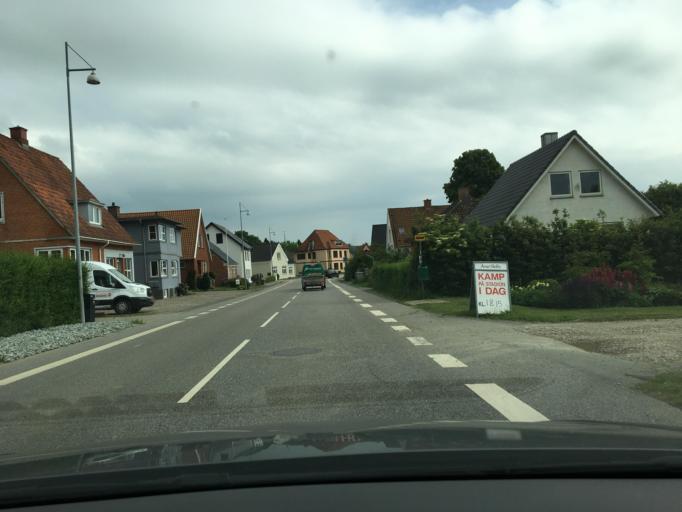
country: DK
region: South Denmark
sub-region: Middelfart Kommune
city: Norre Aby
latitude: 55.4784
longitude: 9.8102
